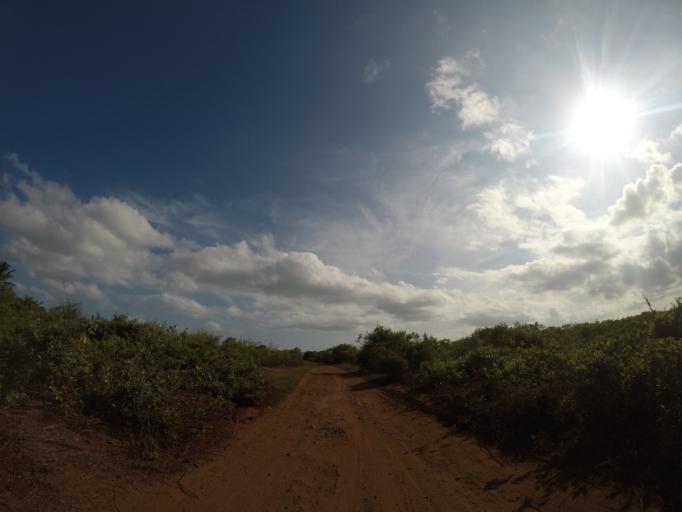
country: TZ
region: Zanzibar Central/South
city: Koani
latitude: -6.2072
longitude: 39.3141
